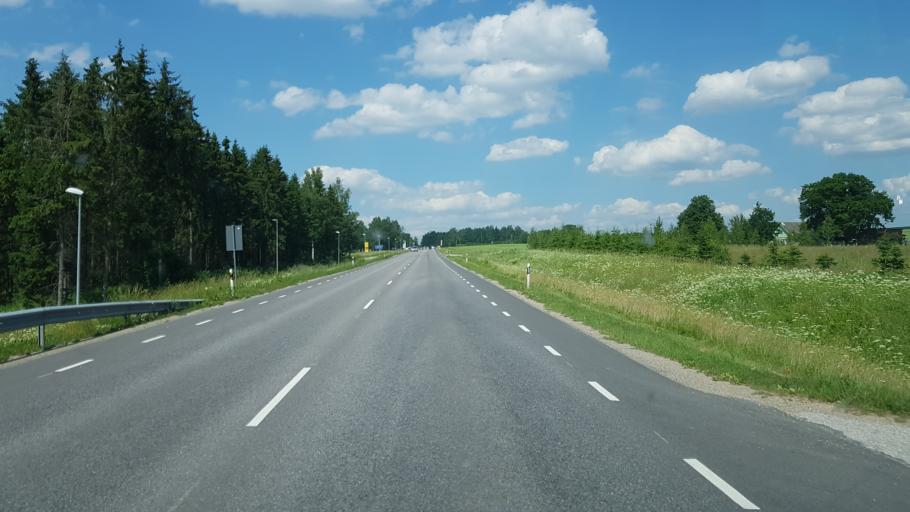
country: EE
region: Jogevamaa
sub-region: Tabivere vald
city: Tabivere
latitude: 58.4865
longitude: 26.6818
